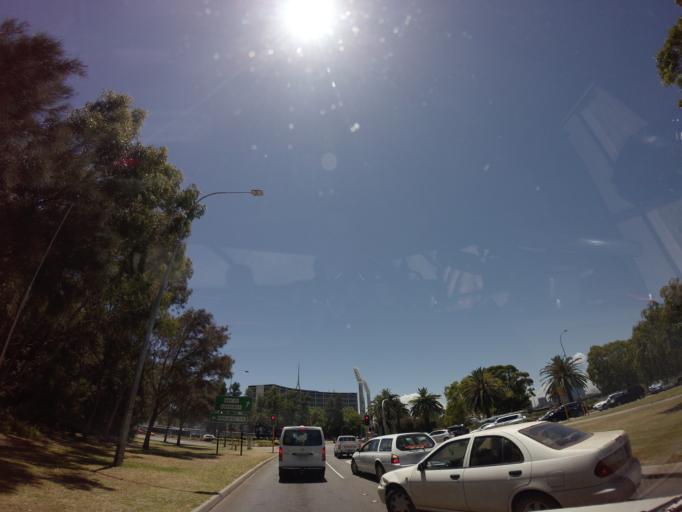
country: AU
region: Western Australia
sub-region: City of Perth
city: East Perth
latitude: -31.9628
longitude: 115.8782
